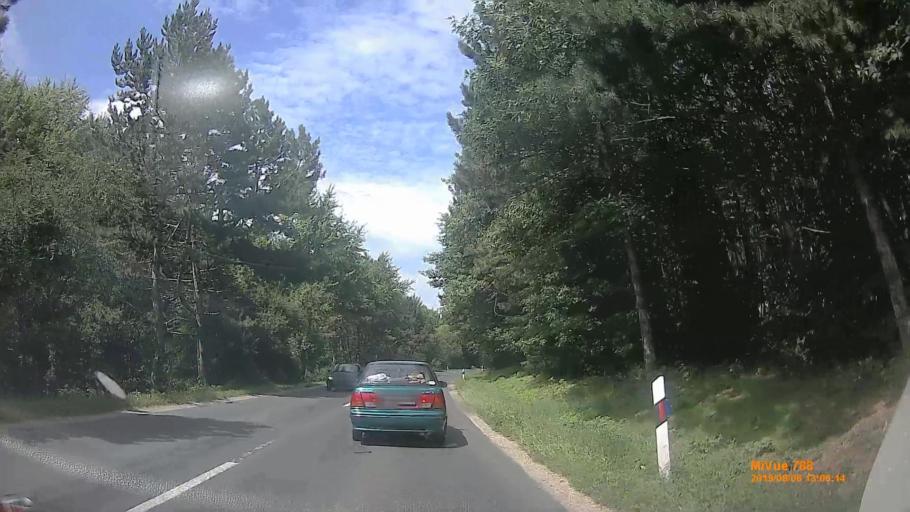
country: HU
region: Vas
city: Koszeg
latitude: 47.3717
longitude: 16.5621
